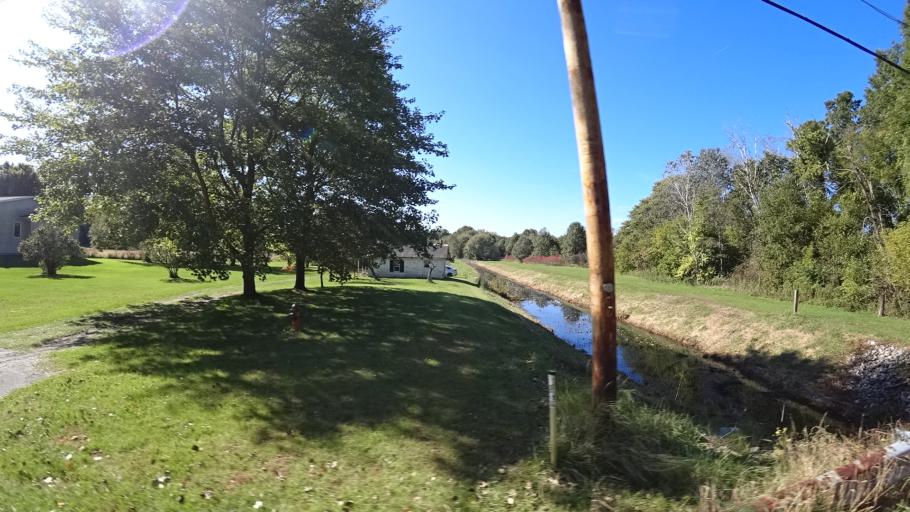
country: US
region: Indiana
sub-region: LaPorte County
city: Long Beach
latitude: 41.7416
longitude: -86.8162
